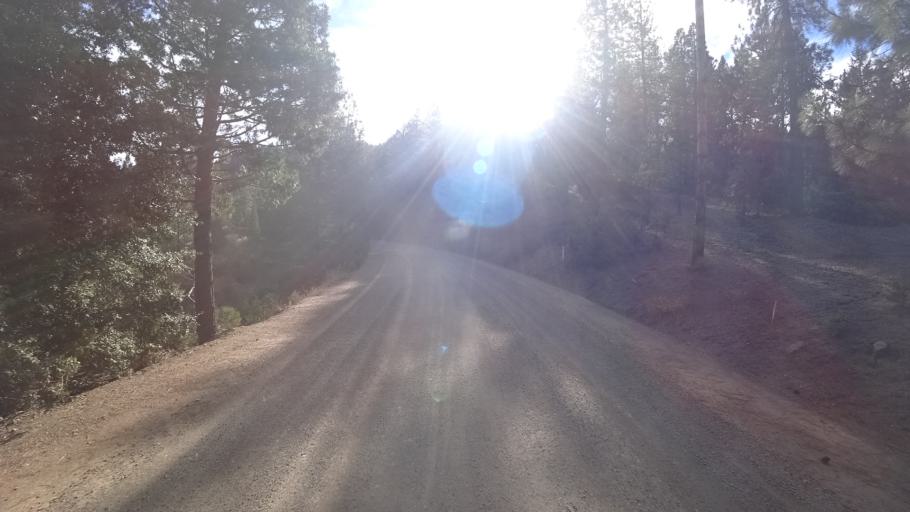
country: US
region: California
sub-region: Siskiyou County
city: Yreka
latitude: 41.7153
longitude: -122.7904
